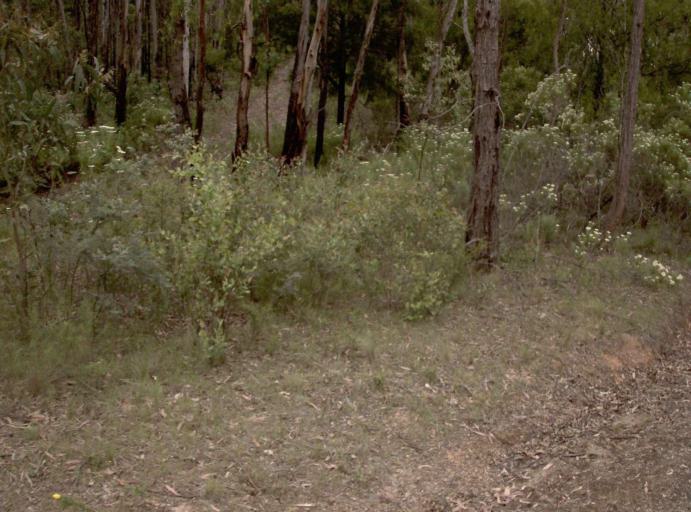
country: AU
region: Victoria
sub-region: East Gippsland
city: Bairnsdale
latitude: -37.6524
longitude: 147.2784
